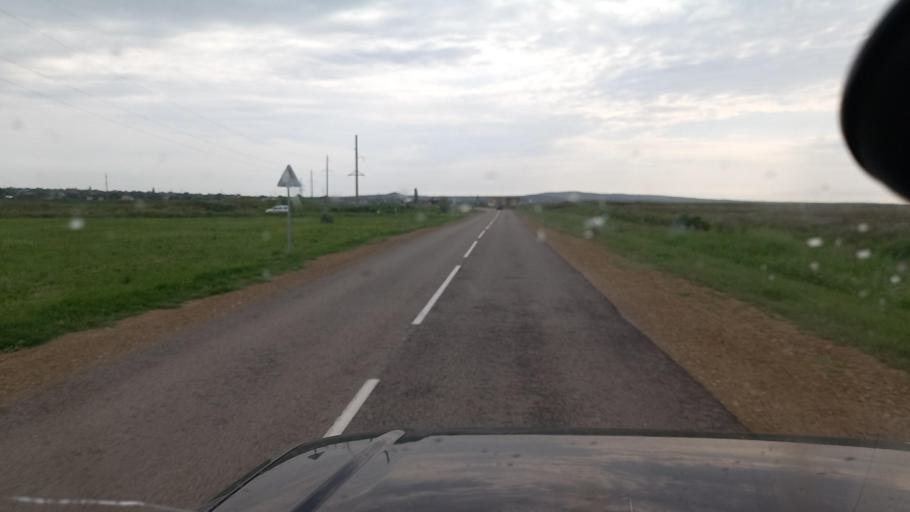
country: RU
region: Krasnodarskiy
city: Akhtanizovskaya
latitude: 45.3416
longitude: 37.1190
